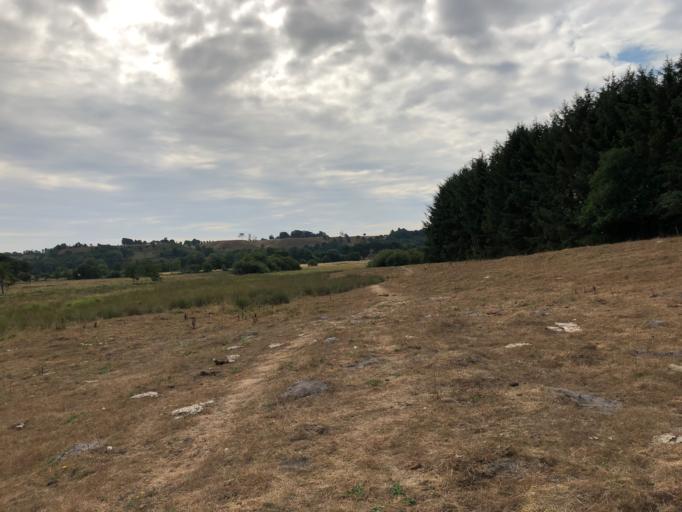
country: DK
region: South Denmark
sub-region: Vejle Kommune
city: Egtved
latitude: 55.6505
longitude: 9.2780
